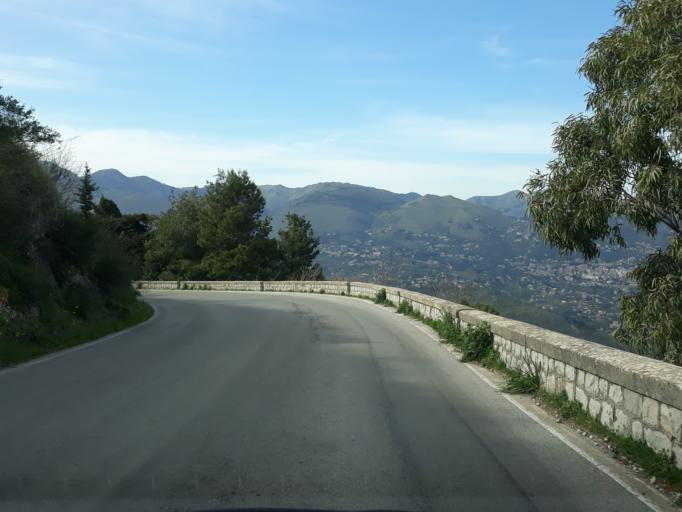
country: IT
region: Sicily
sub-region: Palermo
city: Piano Maglio-Blandino
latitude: 38.0446
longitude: 13.3086
